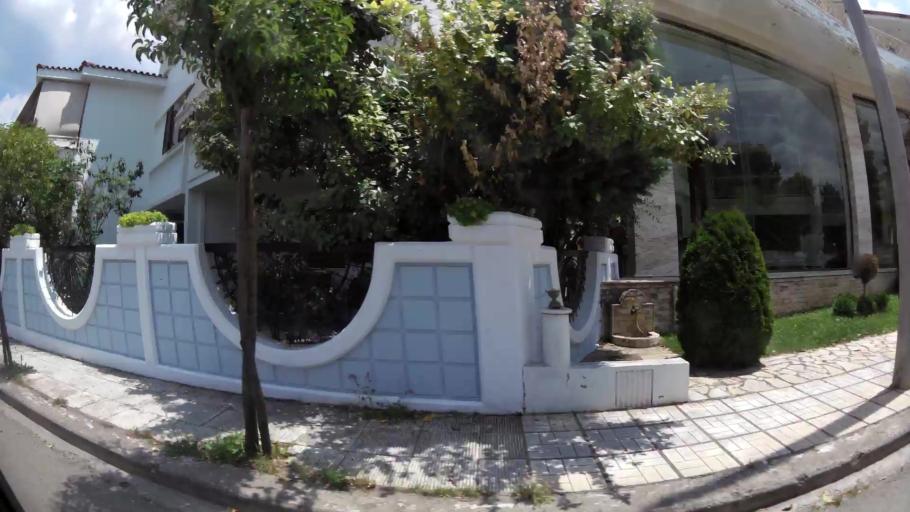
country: GR
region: West Macedonia
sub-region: Nomos Kozanis
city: Kozani
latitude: 40.2905
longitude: 21.7818
